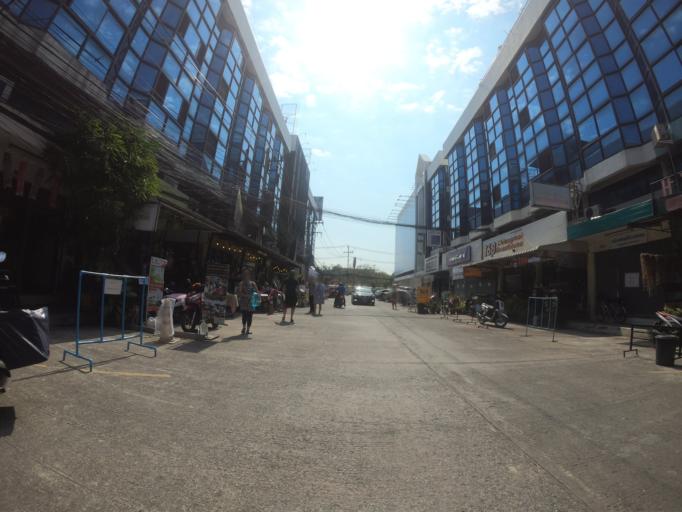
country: TH
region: Chiang Mai
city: Chiang Mai
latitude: 18.7966
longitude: 98.9839
